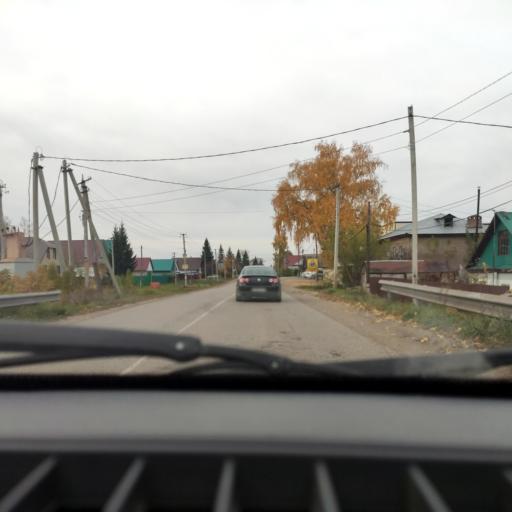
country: RU
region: Bashkortostan
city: Avdon
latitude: 54.6552
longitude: 55.7639
